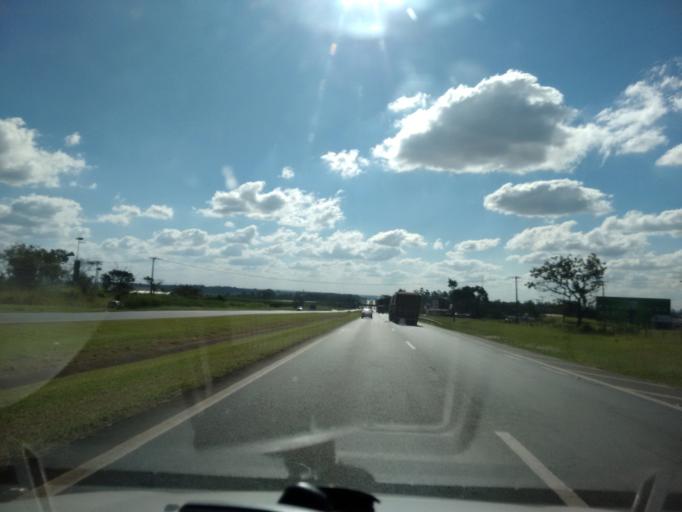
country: BR
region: Sao Paulo
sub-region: Araraquara
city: Araraquara
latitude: -21.8387
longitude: -48.1501
